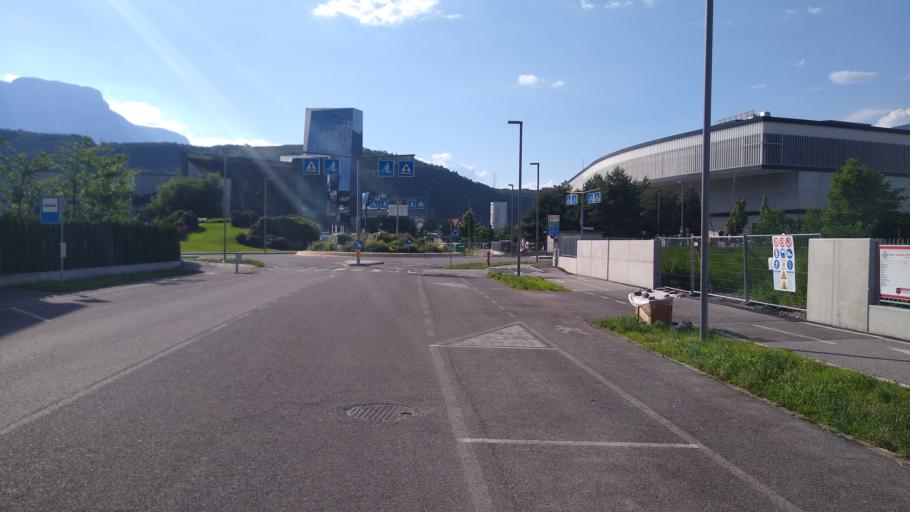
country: IT
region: Trentino-Alto Adige
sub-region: Bolzano
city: San Giacomo
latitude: 46.4694
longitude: 11.3168
